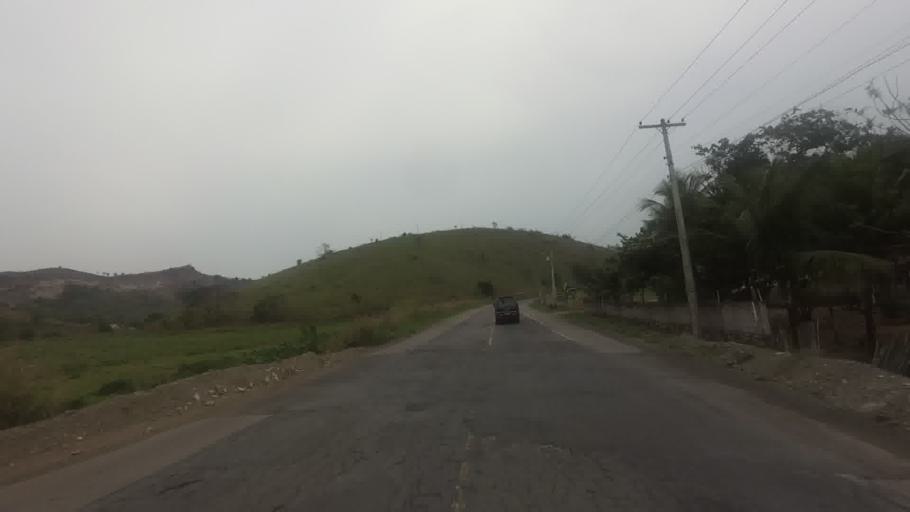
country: BR
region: Rio de Janeiro
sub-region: Santo Antonio De Padua
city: Santo Antonio de Padua
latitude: -21.6034
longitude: -42.2403
